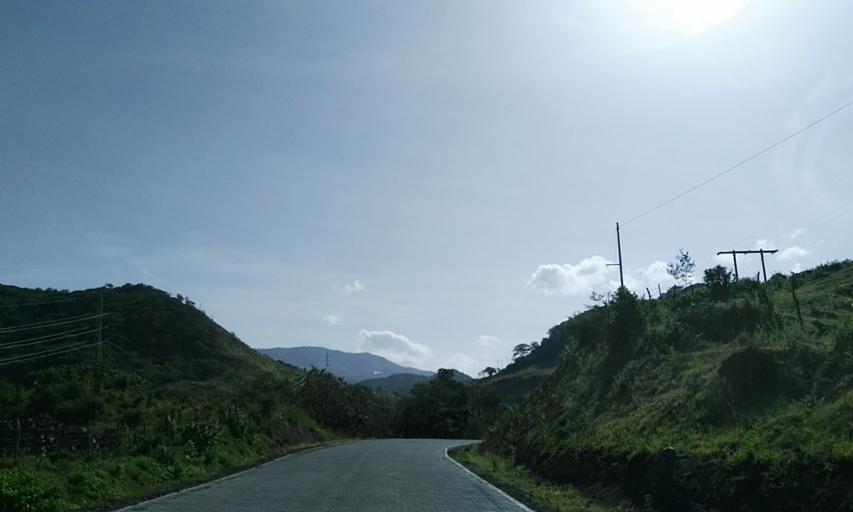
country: NI
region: Matagalpa
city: Ciudad Dario
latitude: 12.7359
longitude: -86.0508
